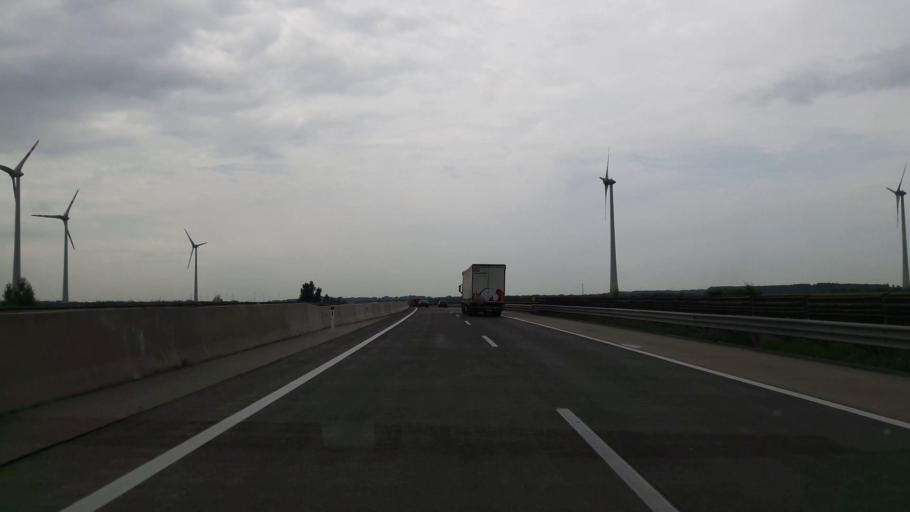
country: AT
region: Burgenland
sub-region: Politischer Bezirk Neusiedl am See
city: Pama
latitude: 48.0526
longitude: 16.9958
